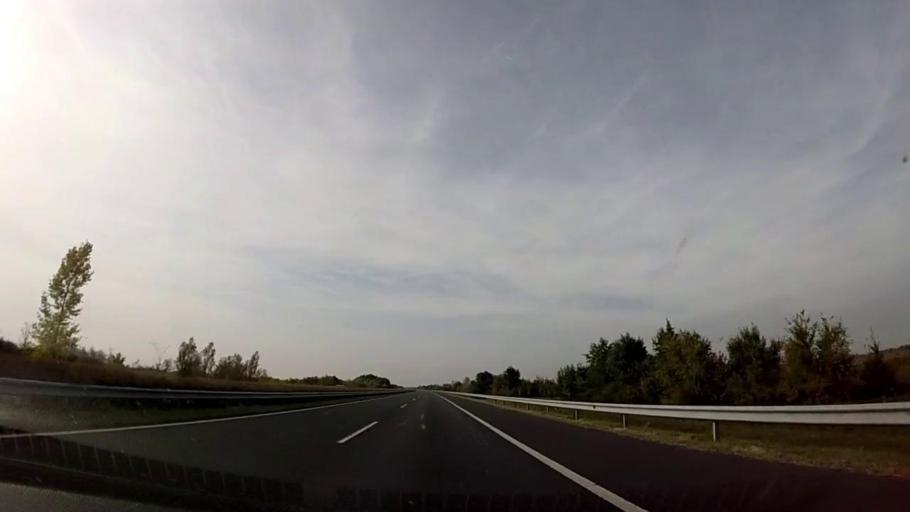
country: HU
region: Somogy
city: Fonyod
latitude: 46.7432
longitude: 17.6094
